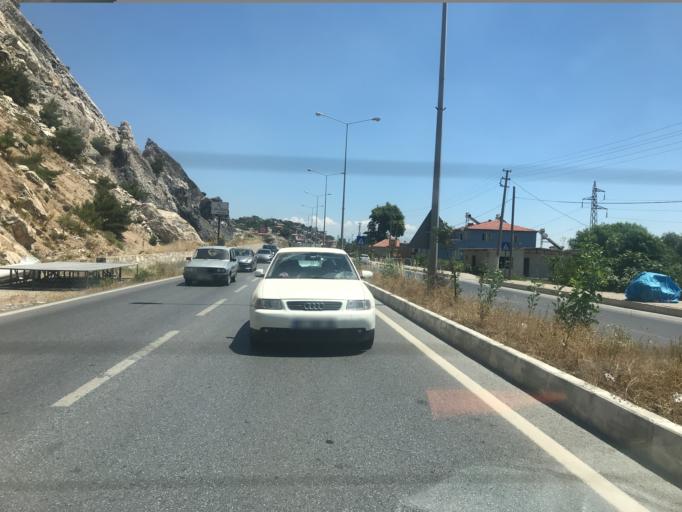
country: TR
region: Aydin
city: Soeke
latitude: 37.7808
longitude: 27.4554
